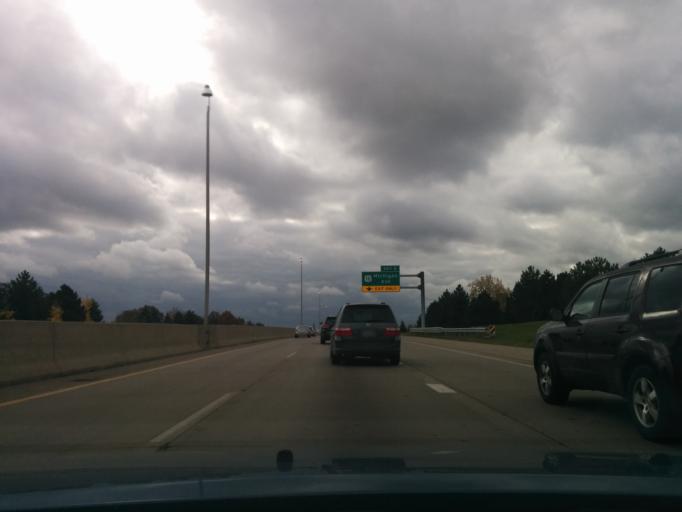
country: US
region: Michigan
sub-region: Wayne County
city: Dearborn
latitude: 42.3202
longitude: -83.2154
